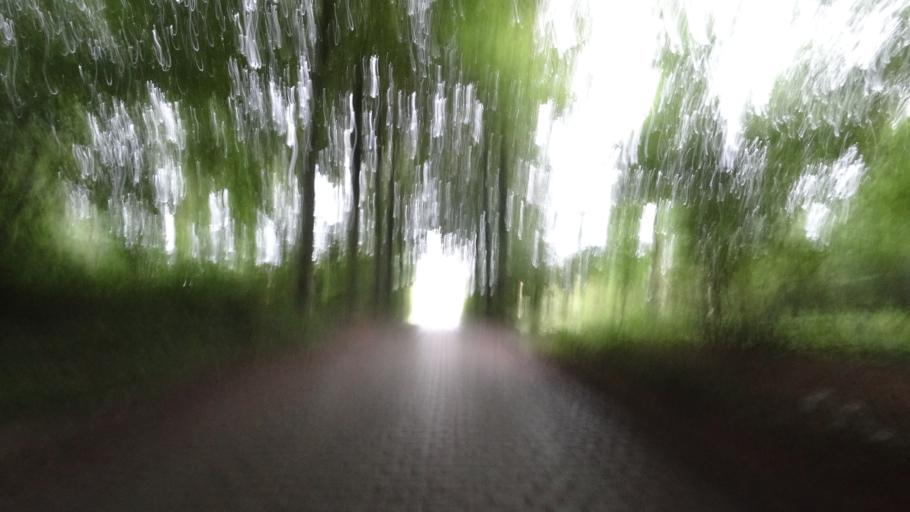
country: BE
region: Wallonia
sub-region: Province du Brabant Wallon
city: Walhain-Saint-Paul
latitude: 50.6109
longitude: 4.7366
